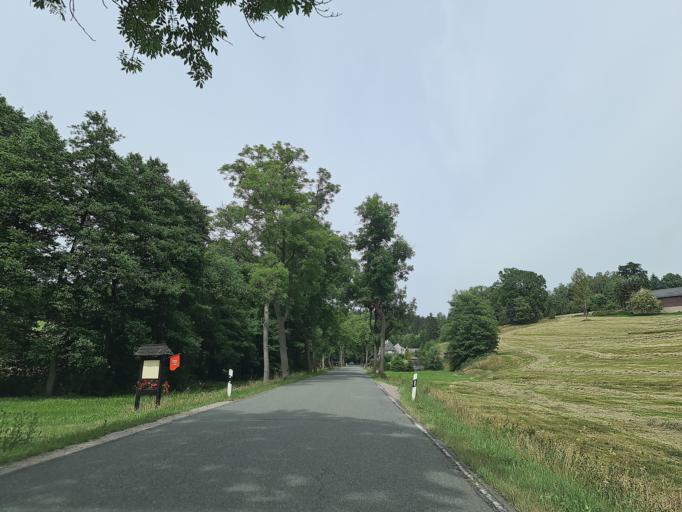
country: DE
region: Saxony
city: Heidersdorf
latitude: 50.6732
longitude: 13.4210
